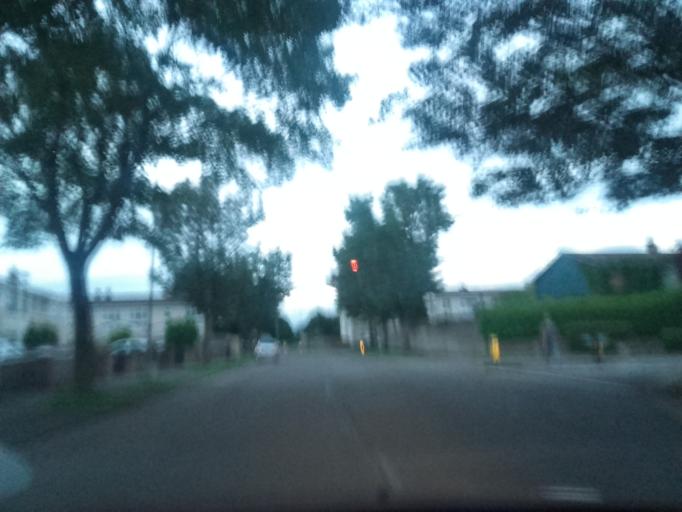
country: IE
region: Leinster
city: Tallaght
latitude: 53.2882
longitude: -6.3830
